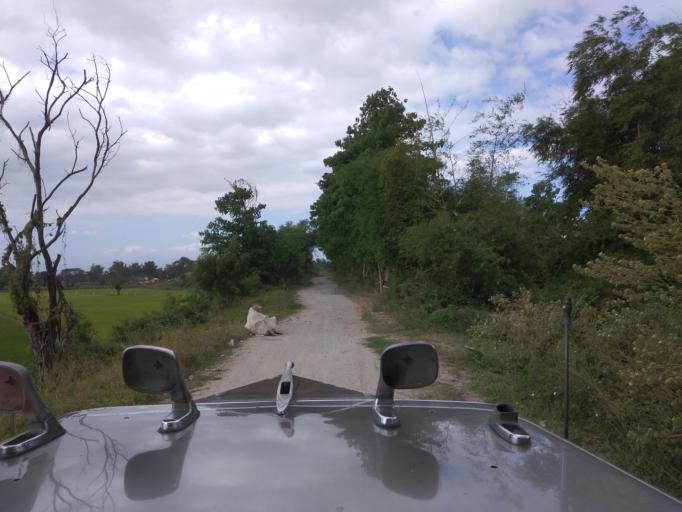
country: PH
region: Central Luzon
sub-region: Province of Pampanga
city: San Patricio
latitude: 15.1140
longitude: 120.7166
